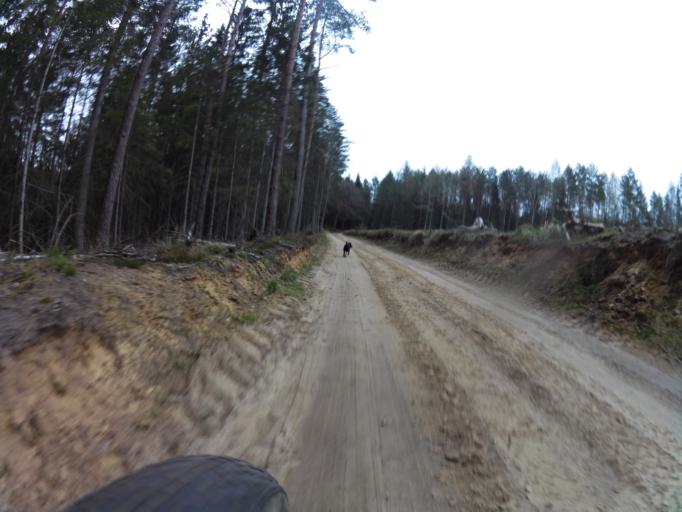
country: PL
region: West Pomeranian Voivodeship
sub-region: Powiat koszalinski
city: Polanow
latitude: 54.1838
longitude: 16.6771
